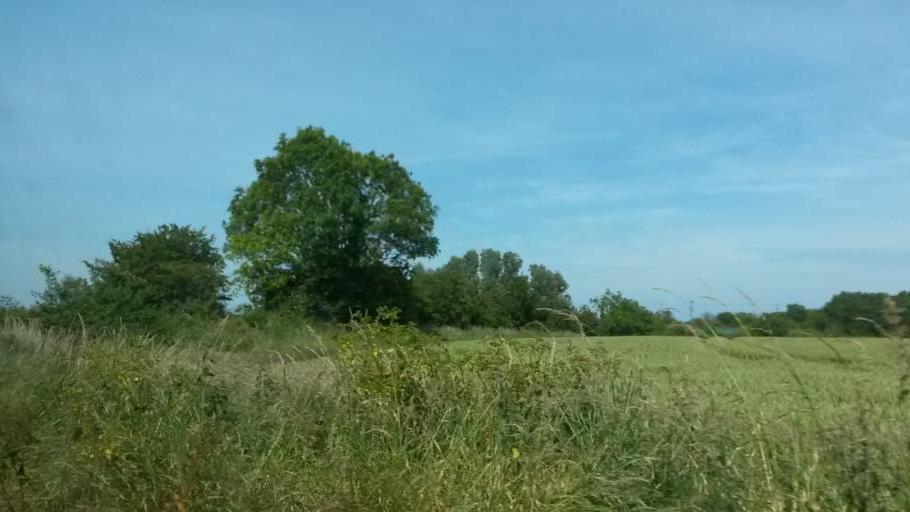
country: IE
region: Leinster
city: Lusk
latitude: 53.5143
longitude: -6.1538
